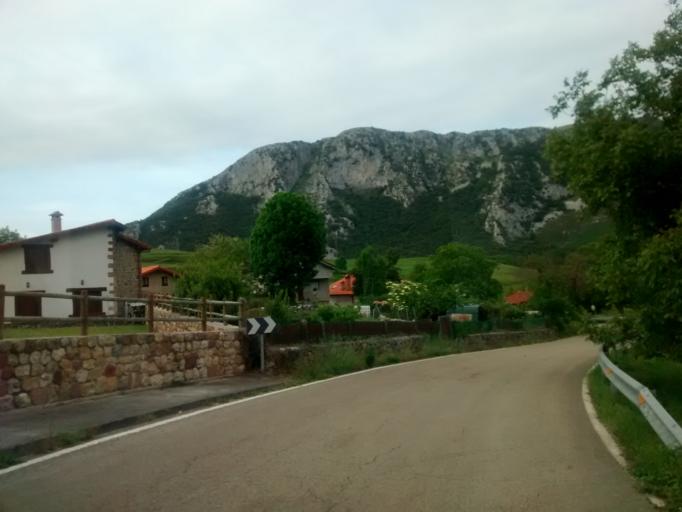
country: ES
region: Cantabria
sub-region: Provincia de Cantabria
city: San Vicente de la Barquera
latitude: 43.2527
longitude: -4.4169
